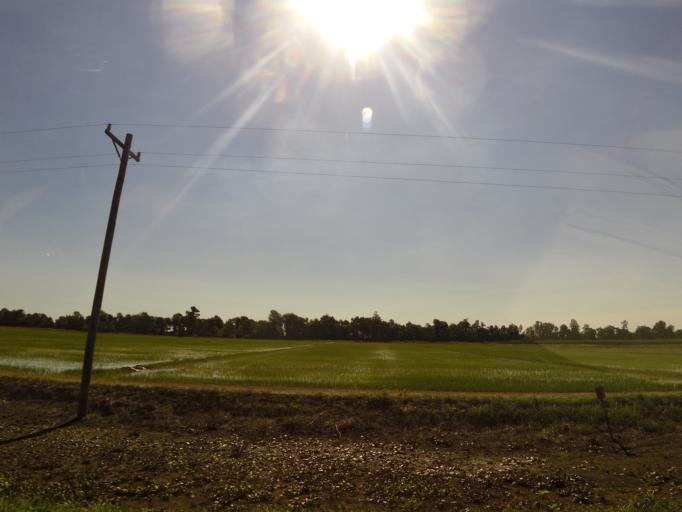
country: US
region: Arkansas
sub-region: Clay County
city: Corning
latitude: 36.4241
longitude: -90.4737
